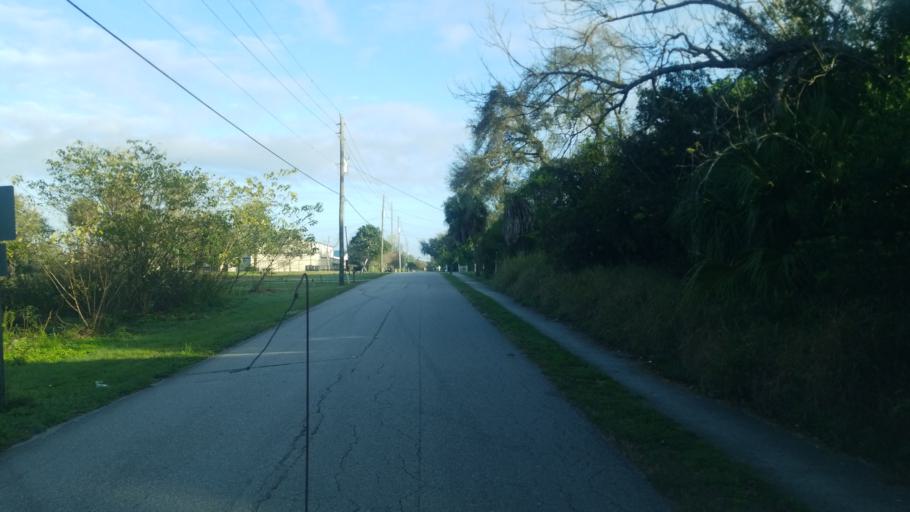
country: US
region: Florida
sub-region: Manatee County
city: Samoset
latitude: 27.4445
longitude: -82.5342
